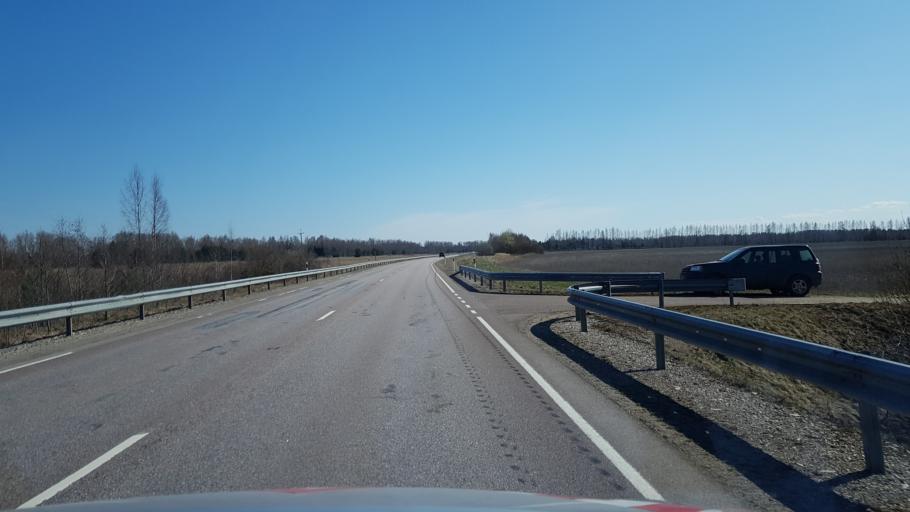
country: EE
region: Jogevamaa
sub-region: Mustvee linn
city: Mustvee
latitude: 58.8032
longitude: 26.9400
